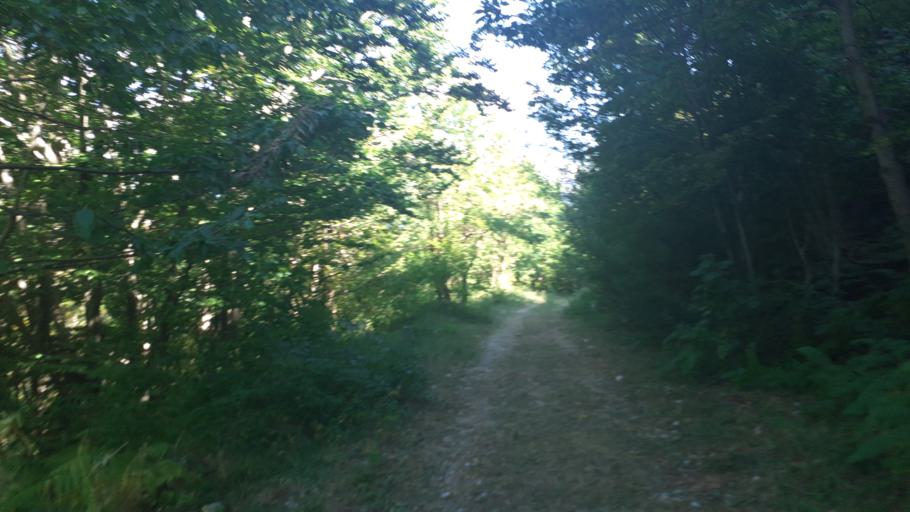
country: IT
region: Abruzzo
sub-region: Provincia di Pescara
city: Sant'Eufemia a Maiella
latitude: 42.1066
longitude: 14.0027
